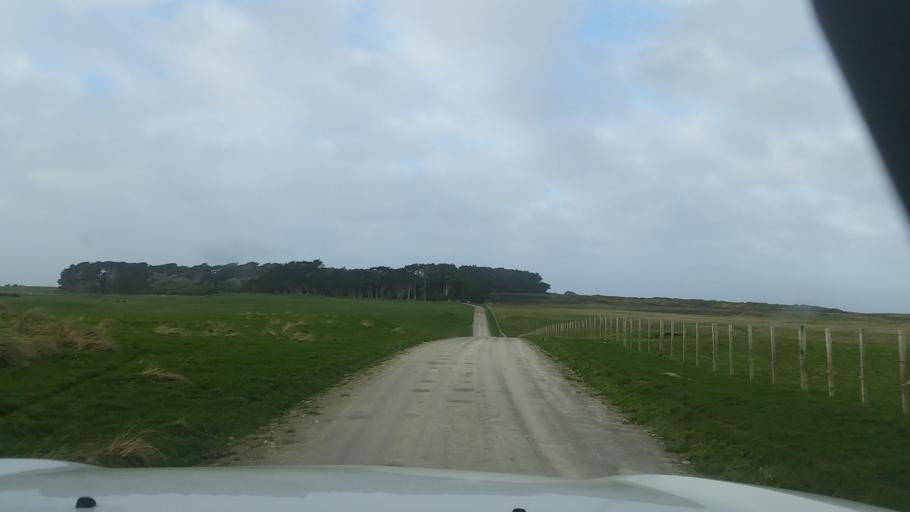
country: NZ
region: Chatham Islands
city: Waitangi
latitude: -43.7378
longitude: -176.2558
